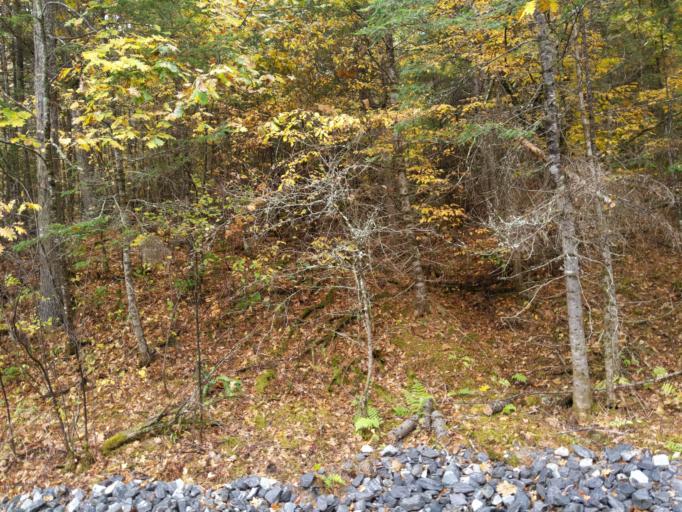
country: US
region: Maine
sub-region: Lincoln County
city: Whitefield
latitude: 44.1024
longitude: -69.6185
